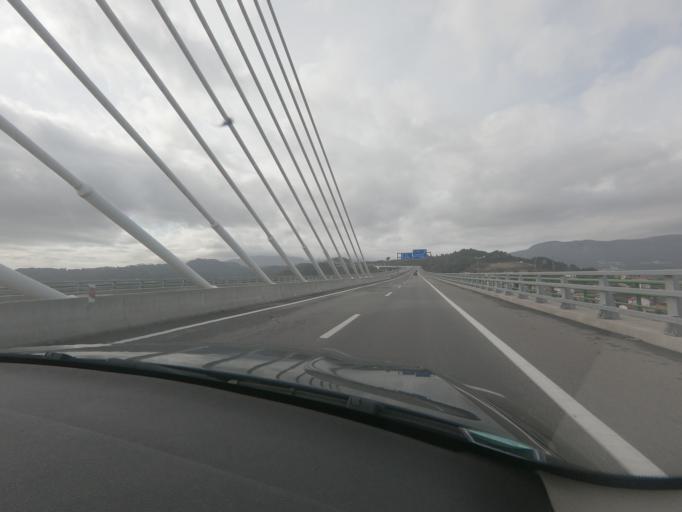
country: PT
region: Vila Real
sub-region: Vila Real
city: Vila Real
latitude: 41.2786
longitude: -7.7530
